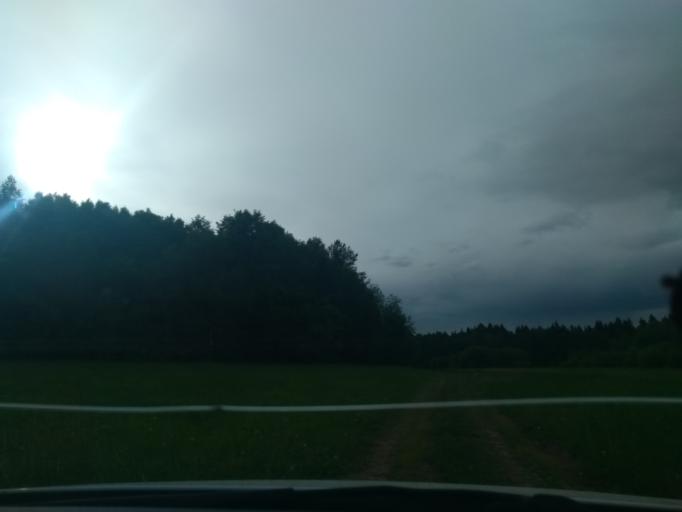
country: RU
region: Perm
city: Ferma
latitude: 57.9809
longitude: 56.3366
